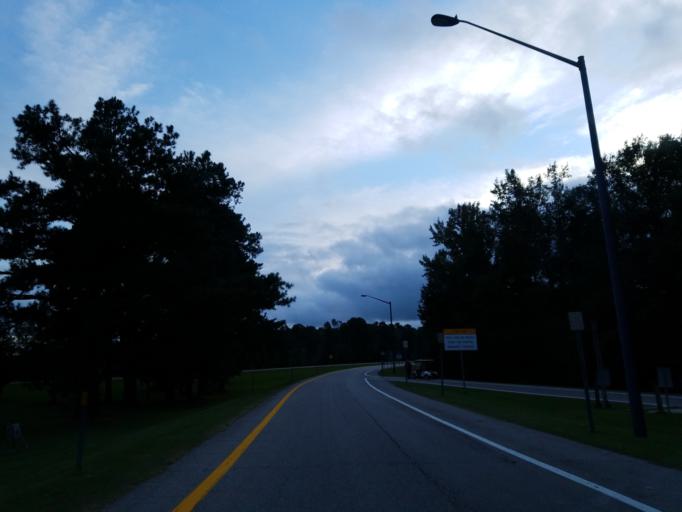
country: US
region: Mississippi
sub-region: Lauderdale County
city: Marion
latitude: 32.4105
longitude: -88.5360
